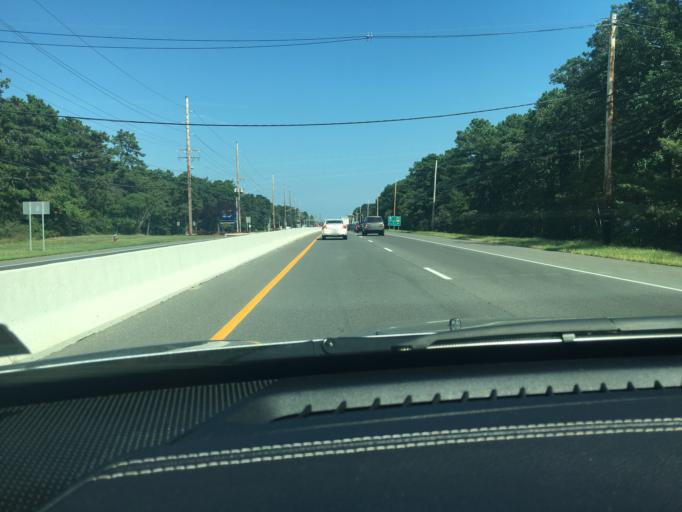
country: US
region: New Jersey
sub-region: Ocean County
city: Leisure Village
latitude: 40.0523
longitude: -74.1833
